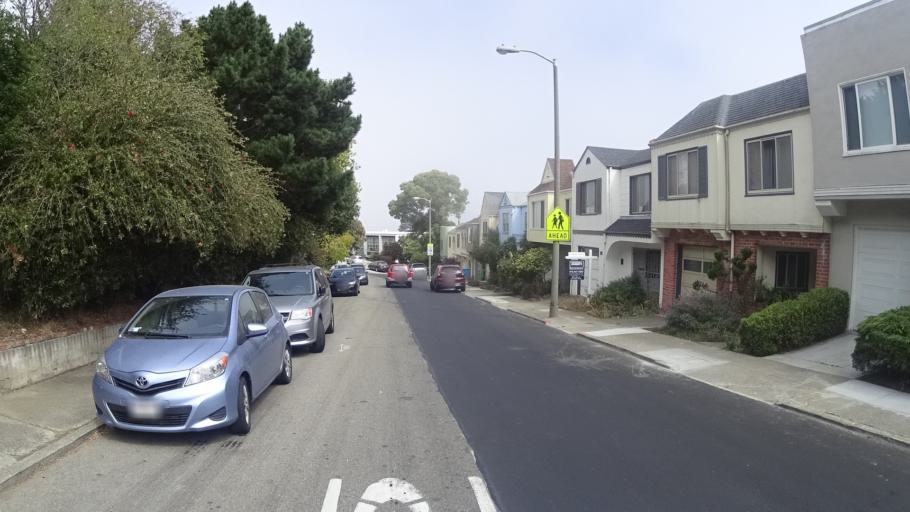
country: US
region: California
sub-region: San Mateo County
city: Daly City
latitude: 37.7378
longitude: -122.4514
